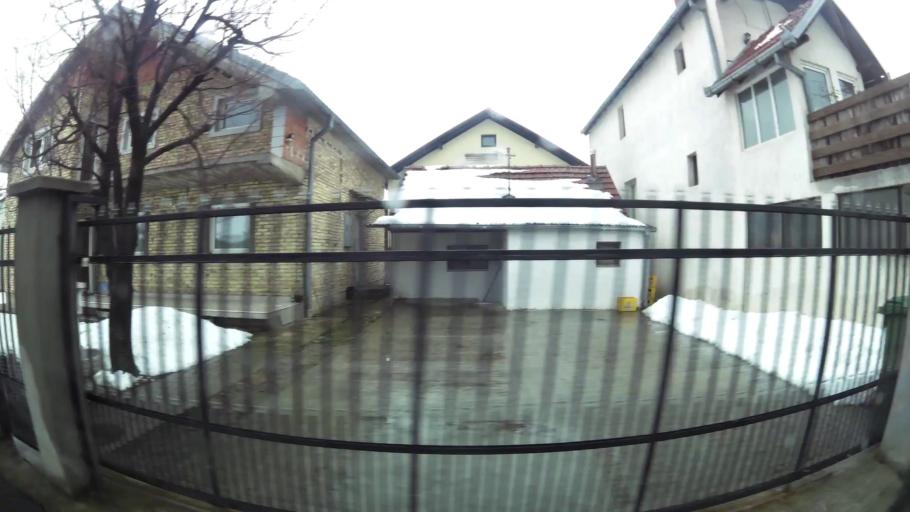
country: RS
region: Central Serbia
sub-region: Belgrade
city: Zemun
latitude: 44.8431
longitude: 20.3663
